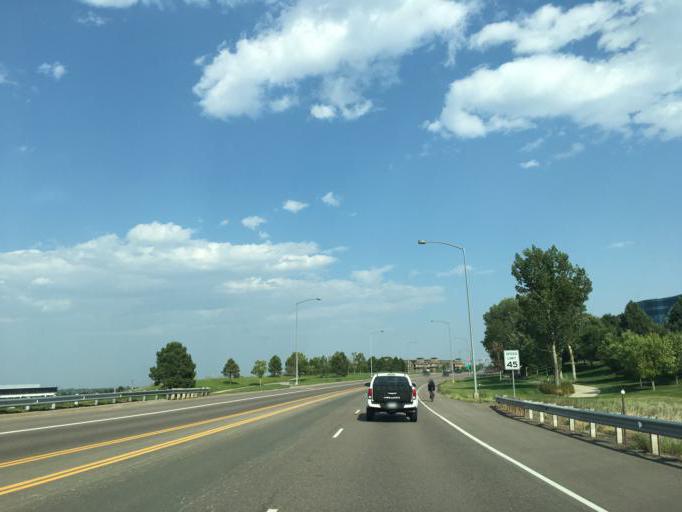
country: US
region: Colorado
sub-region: Broomfield County
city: Broomfield
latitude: 39.9166
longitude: -105.1100
